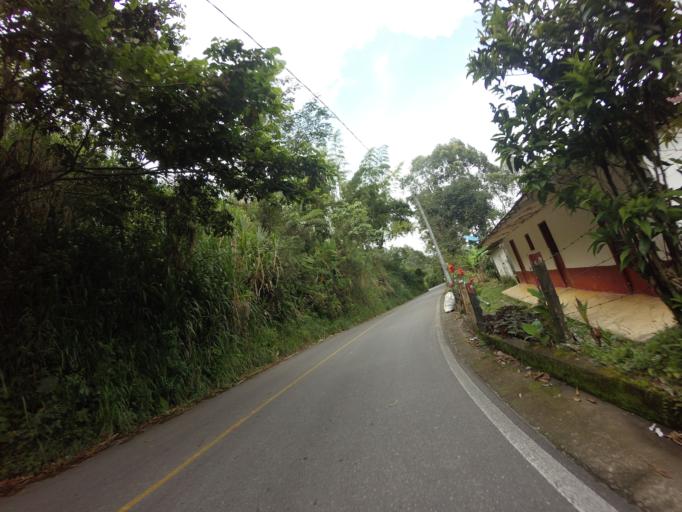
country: CO
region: Caldas
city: Marquetalia
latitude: 5.3014
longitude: -75.0224
